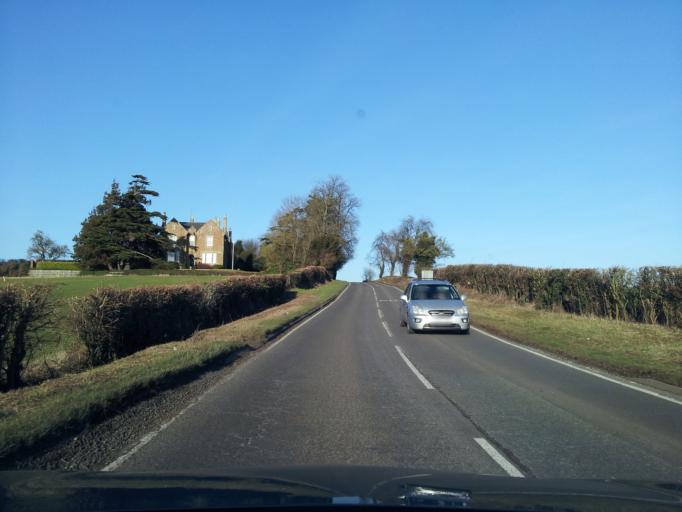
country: GB
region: England
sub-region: Northamptonshire
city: Bugbrooke
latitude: 52.2417
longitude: -0.9734
